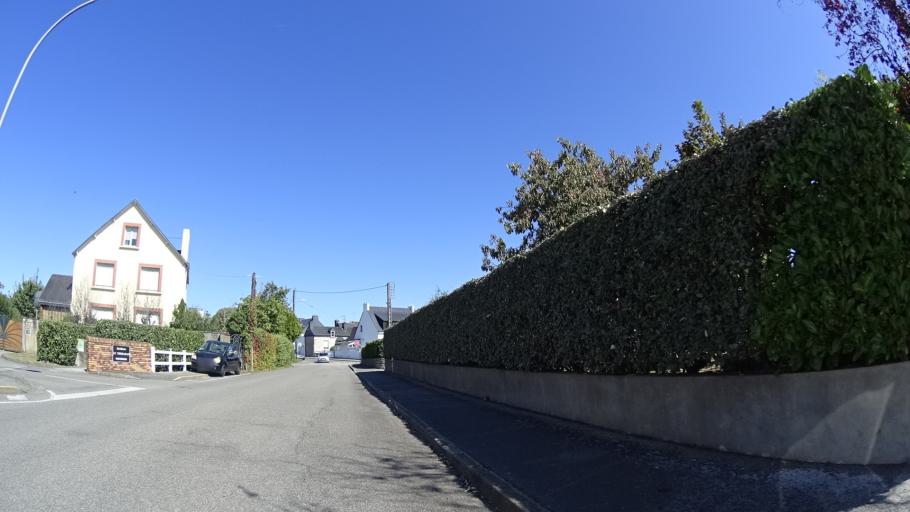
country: FR
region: Brittany
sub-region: Departement du Morbihan
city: Vannes
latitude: 47.6413
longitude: -2.7653
